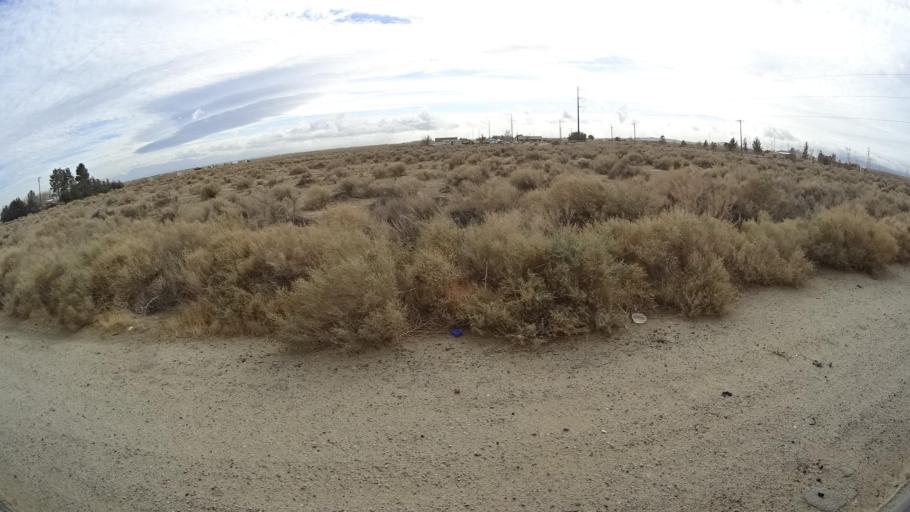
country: US
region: California
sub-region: Kern County
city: Rosamond
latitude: 34.8634
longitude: -118.3082
